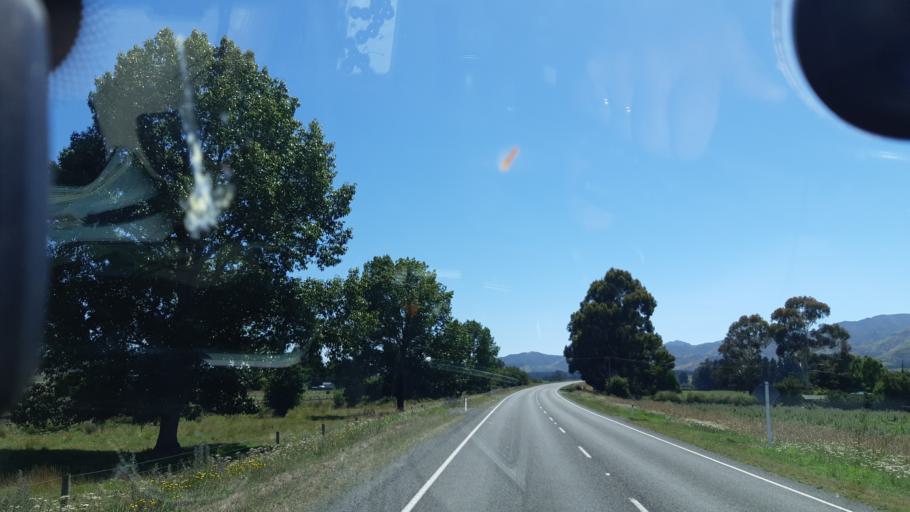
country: NZ
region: Canterbury
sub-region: Kaikoura District
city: Kaikoura
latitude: -42.7093
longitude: 173.2937
